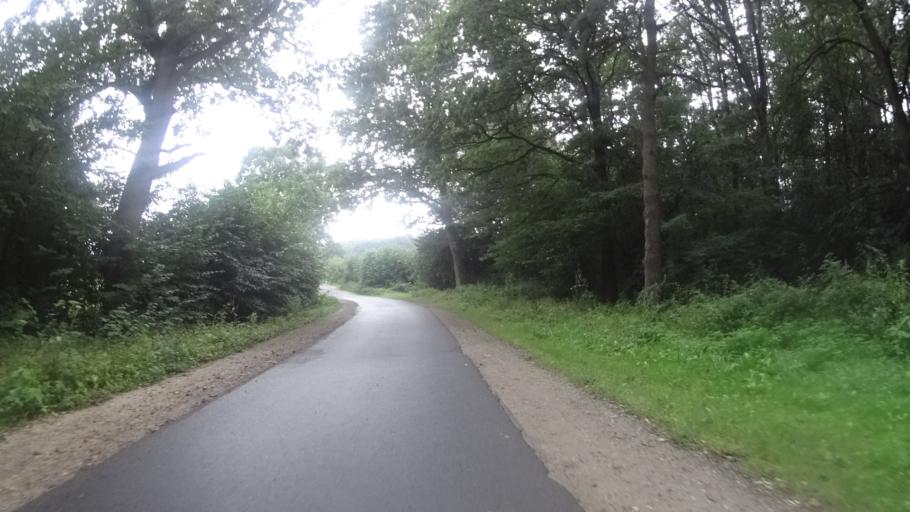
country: DE
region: Schleswig-Holstein
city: Roseburg
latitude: 53.5218
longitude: 10.6270
